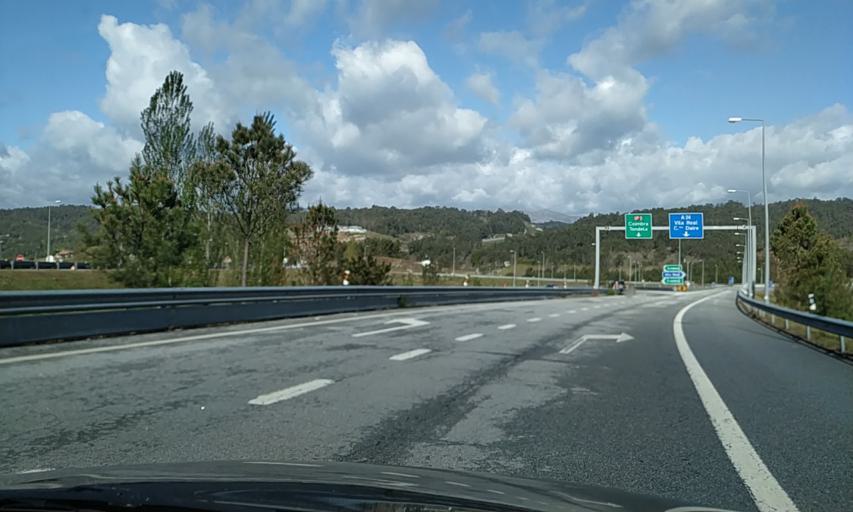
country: PT
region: Viseu
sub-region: Viseu
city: Viseu
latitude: 40.6253
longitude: -7.9572
